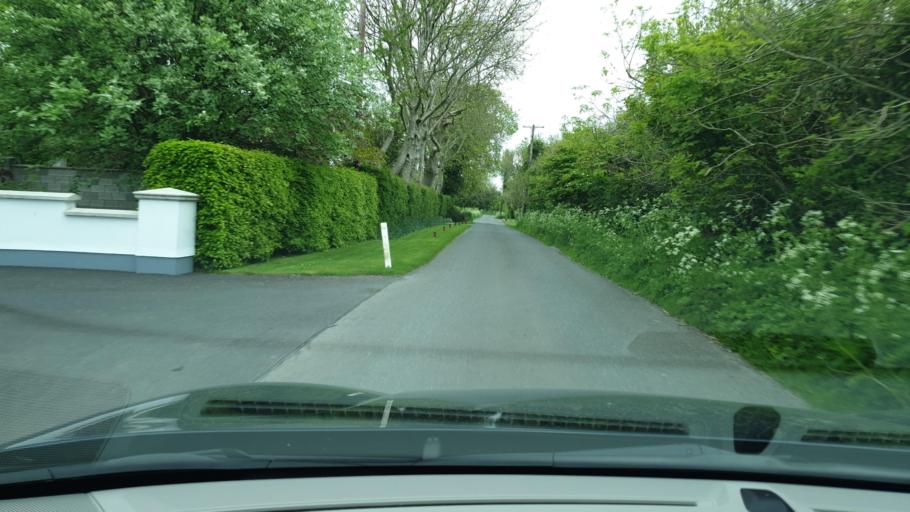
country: IE
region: Leinster
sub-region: An Mhi
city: Ratoath
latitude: 53.5031
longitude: -6.4878
